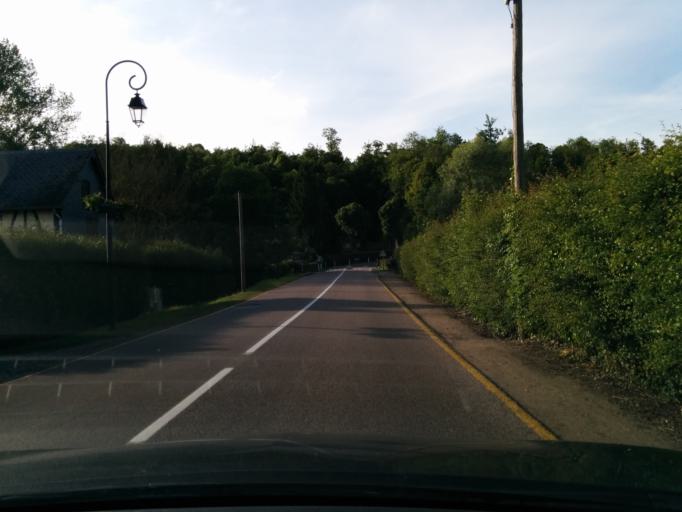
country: FR
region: Haute-Normandie
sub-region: Departement de la Seine-Maritime
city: La Feuillie
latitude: 49.4021
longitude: 1.4785
